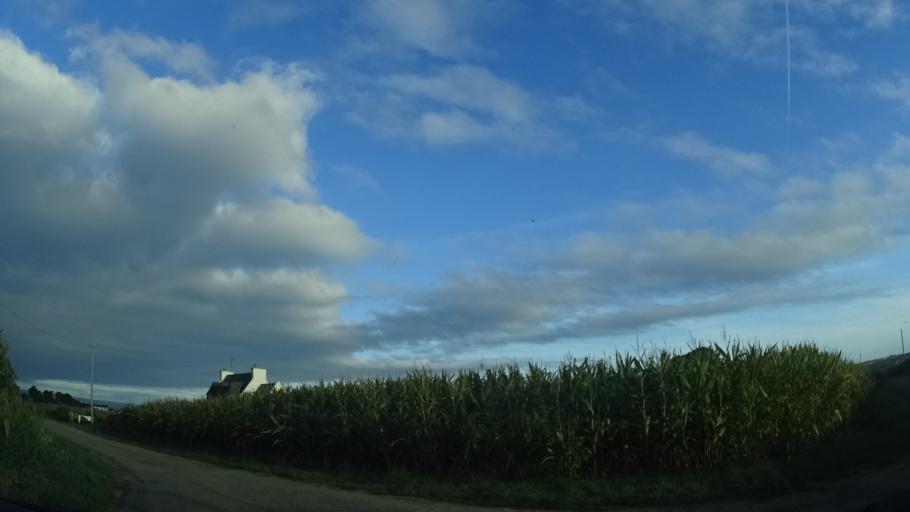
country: FR
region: Brittany
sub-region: Departement du Finistere
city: Lampaul-Plouarzel
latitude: 48.4593
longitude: -4.7531
